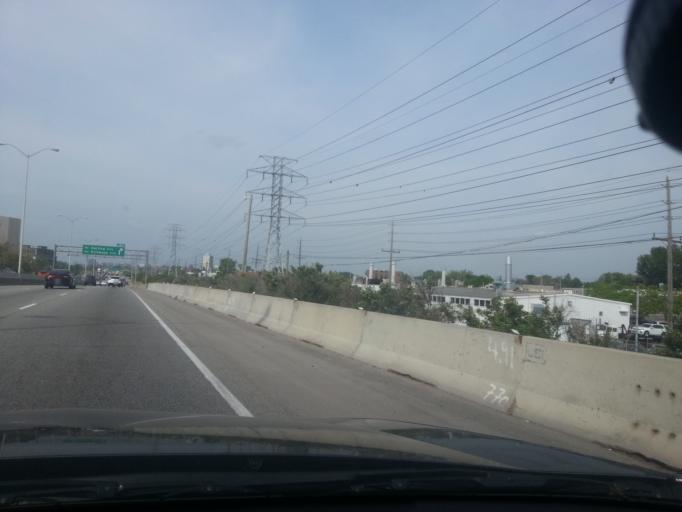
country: CA
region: Ontario
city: Ottawa
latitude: 45.3759
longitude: -75.7482
